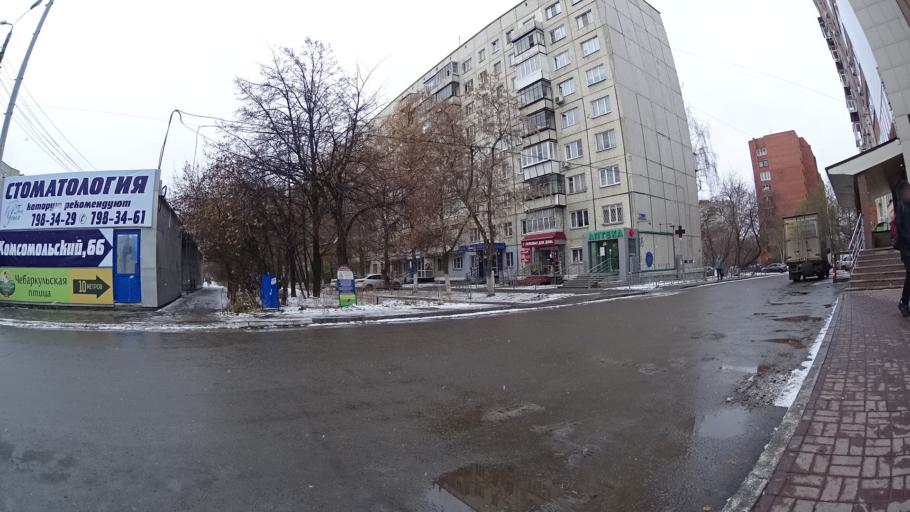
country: RU
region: Chelyabinsk
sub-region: Gorod Chelyabinsk
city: Chelyabinsk
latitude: 55.1947
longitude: 61.3260
